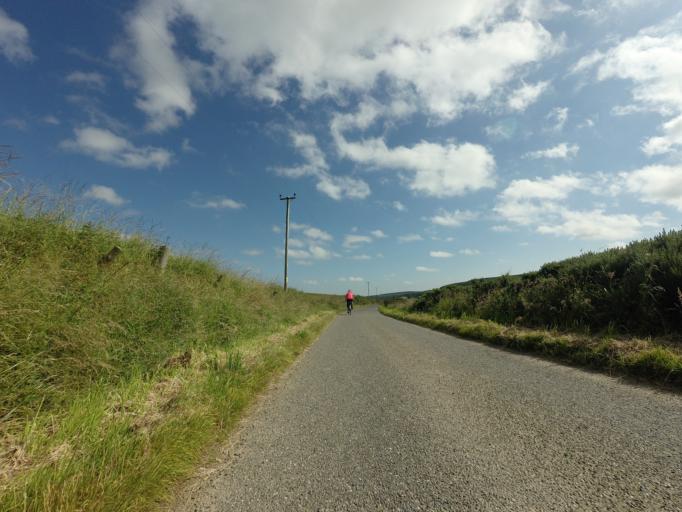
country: GB
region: Scotland
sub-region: Aberdeenshire
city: Turriff
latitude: 57.5797
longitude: -2.5055
